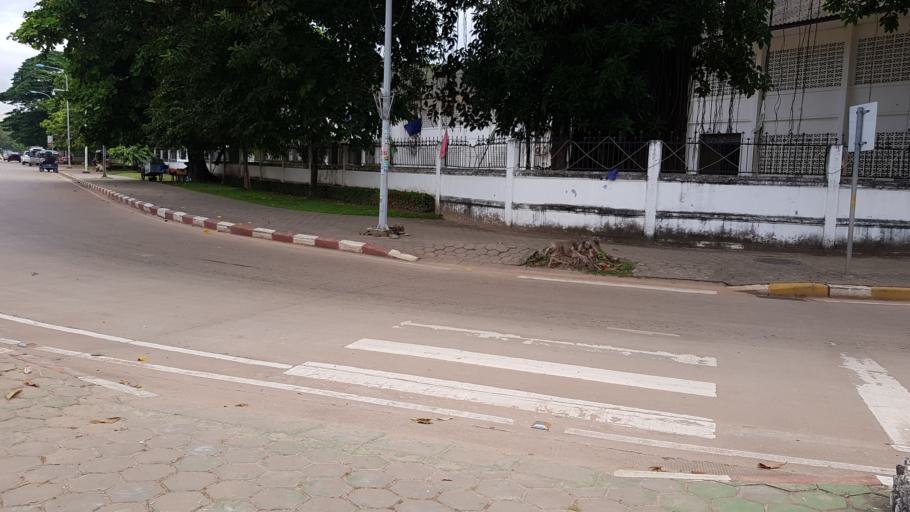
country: LA
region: Vientiane
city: Vientiane
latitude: 17.9698
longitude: 102.6184
